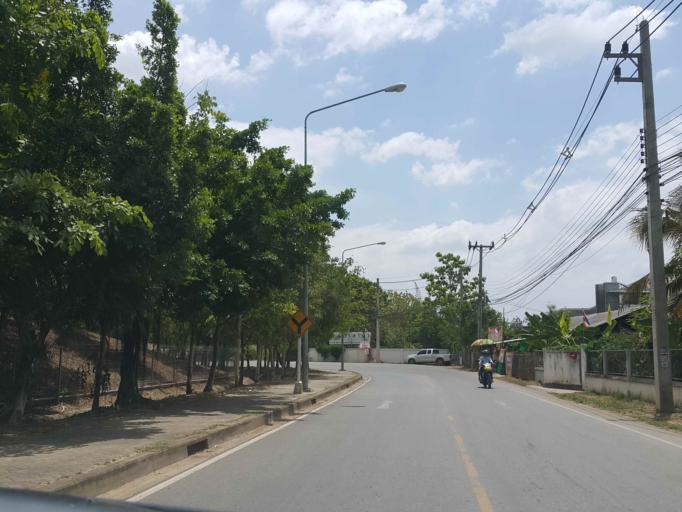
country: TH
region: Chiang Mai
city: Hang Dong
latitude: 18.7497
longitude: 98.9279
